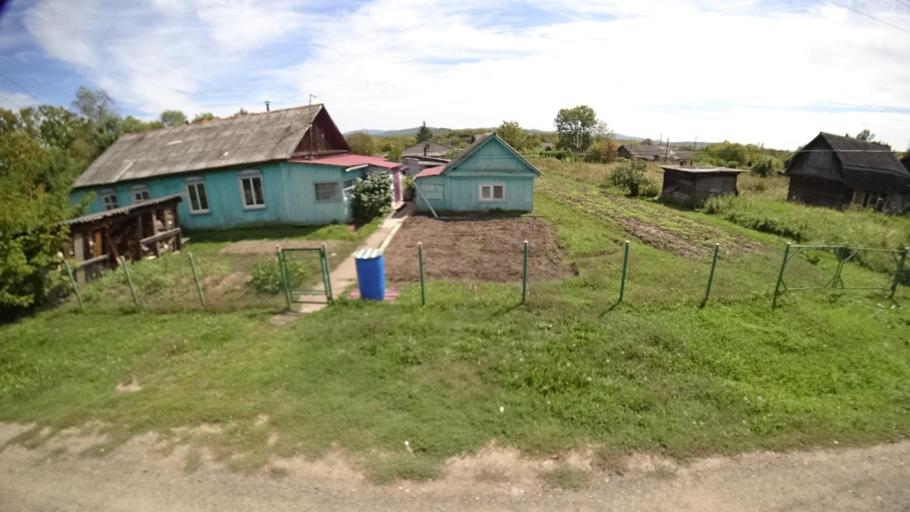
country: RU
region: Primorskiy
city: Yakovlevka
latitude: 44.6442
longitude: 133.5919
